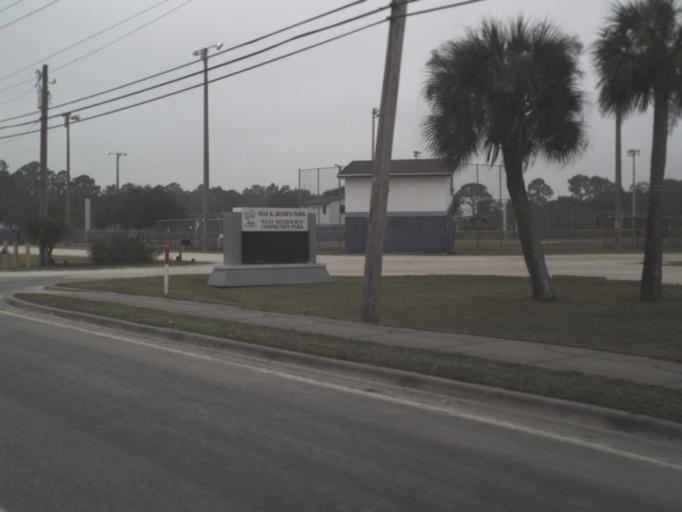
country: US
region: Florida
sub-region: Brevard County
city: June Park
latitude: 28.0596
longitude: -80.6709
